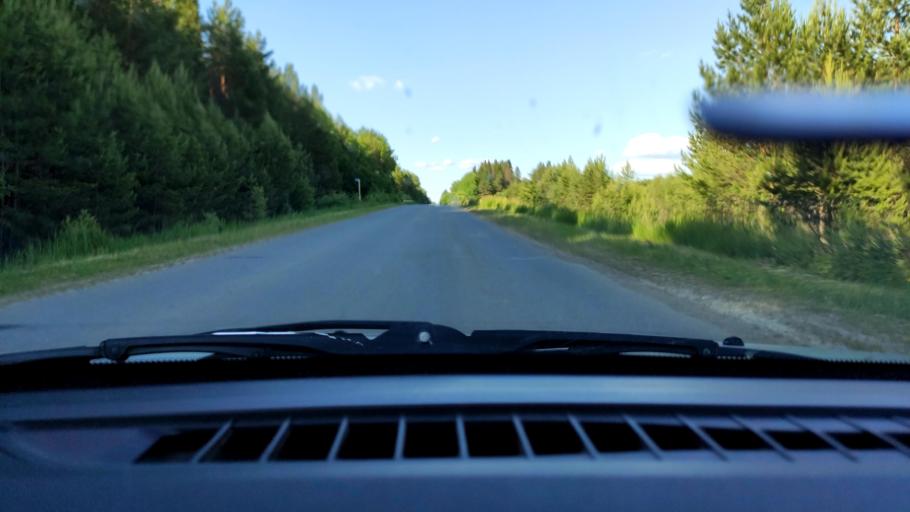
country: RU
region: Perm
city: Uinskoye
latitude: 57.0795
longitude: 56.6122
